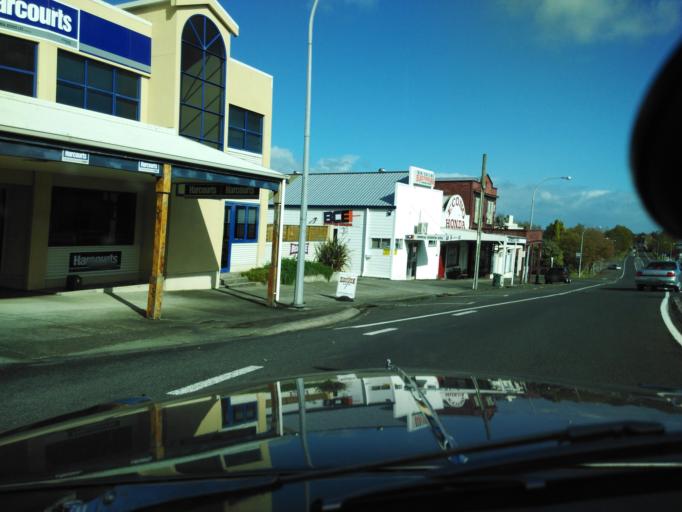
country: NZ
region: Waikato
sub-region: Hauraki District
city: Paeroa
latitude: -37.5433
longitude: 175.7123
